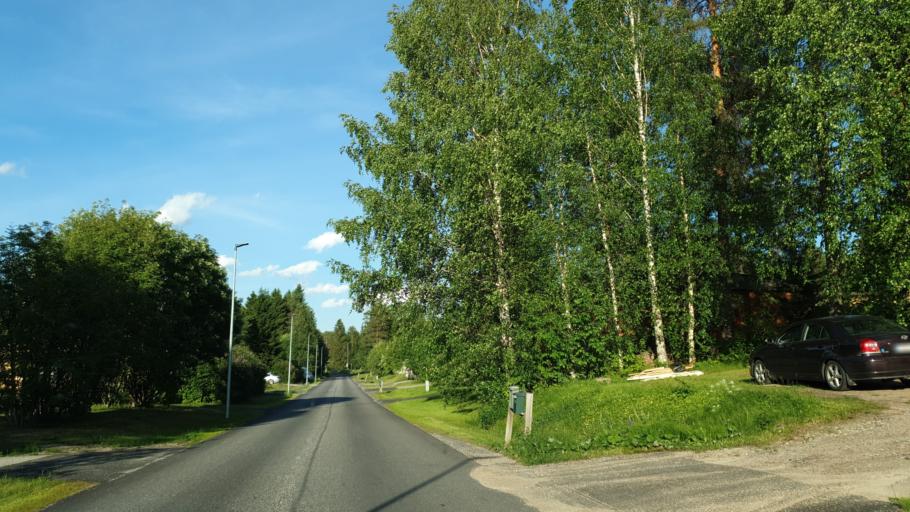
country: FI
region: Kainuu
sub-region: Kehys-Kainuu
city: Kuhmo
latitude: 64.1193
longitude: 29.4950
